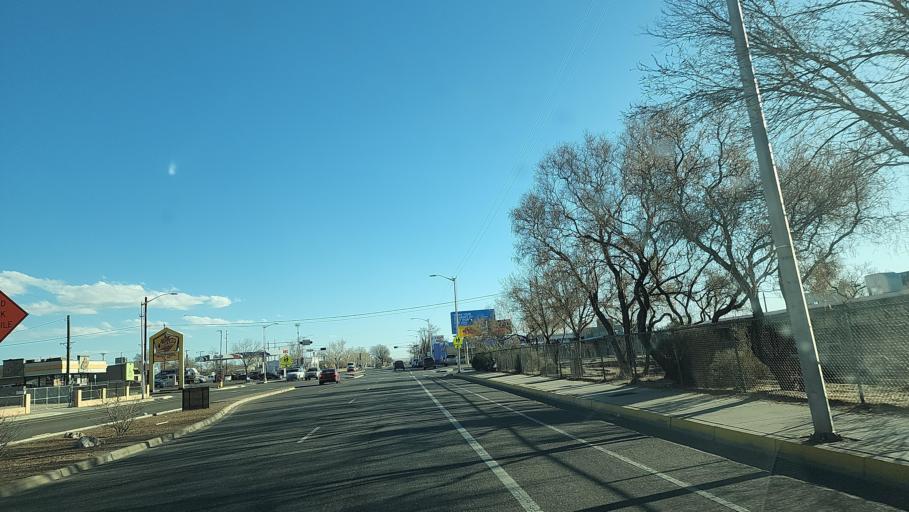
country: US
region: New Mexico
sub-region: Bernalillo County
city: Albuquerque
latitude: 35.0625
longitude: -106.6454
